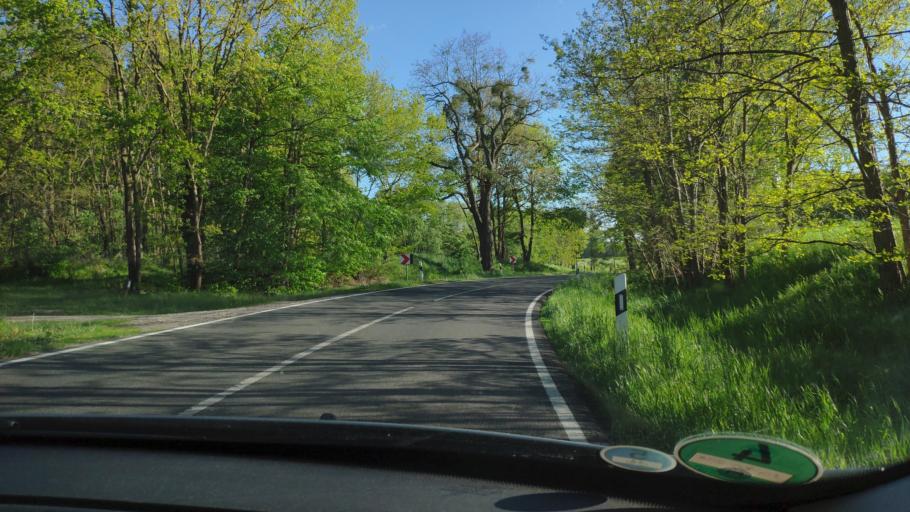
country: DE
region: Mecklenburg-Vorpommern
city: Wesenberg
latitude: 53.3309
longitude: 12.9794
